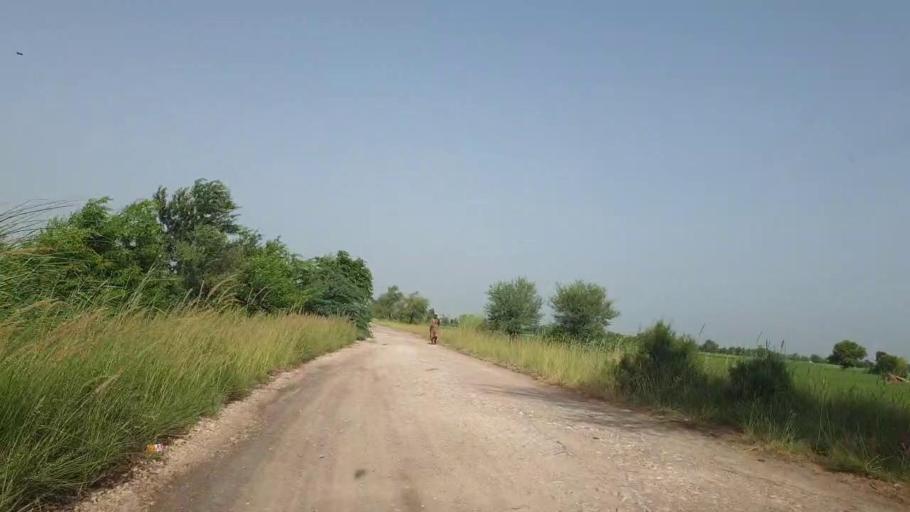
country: PK
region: Sindh
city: Sakrand
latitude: 26.2916
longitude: 68.2256
